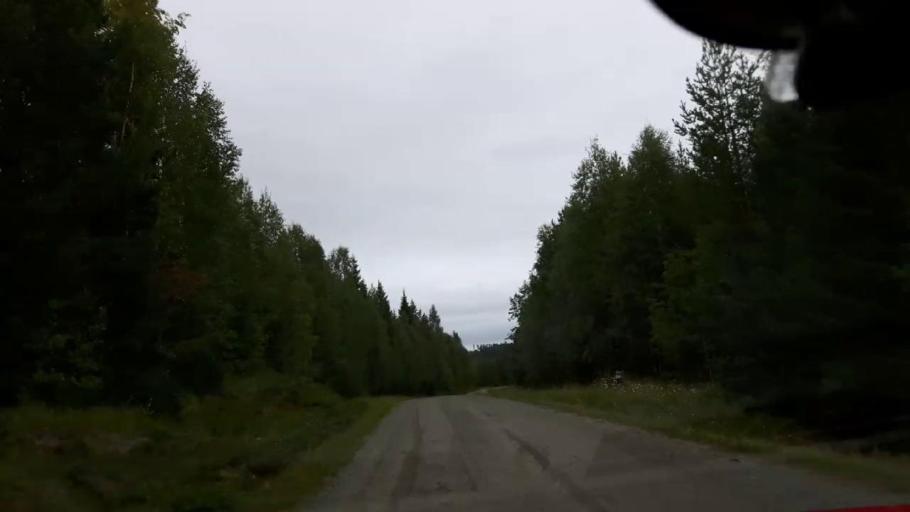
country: SE
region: Vaesternorrland
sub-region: Ange Kommun
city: Fransta
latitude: 62.8562
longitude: 15.9791
